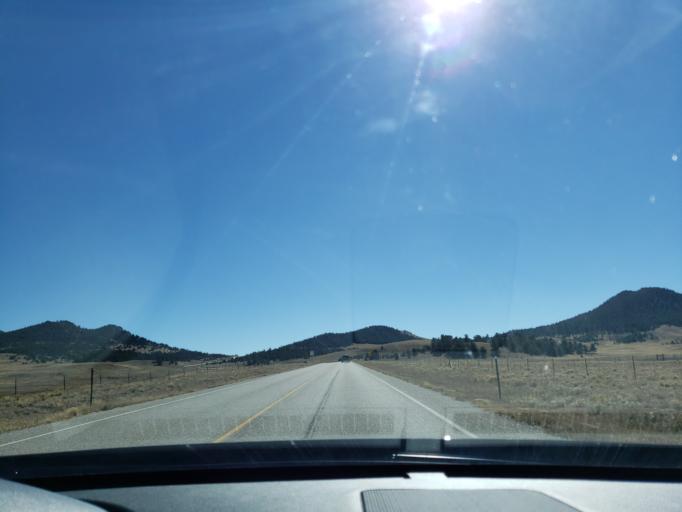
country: US
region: Colorado
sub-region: Chaffee County
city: Salida
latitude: 38.8521
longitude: -105.6520
